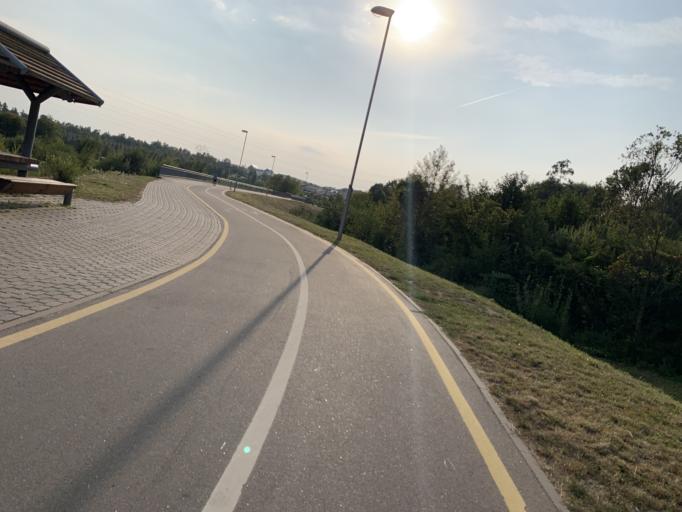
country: BY
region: Minsk
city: Minsk
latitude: 53.8613
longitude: 27.5837
